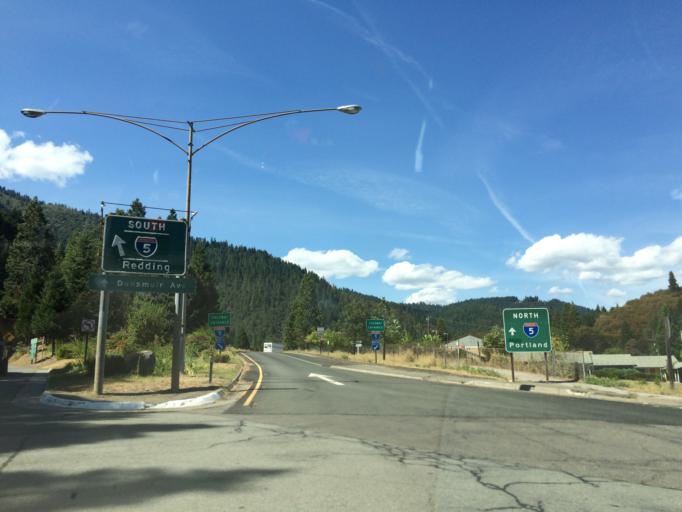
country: US
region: California
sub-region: Siskiyou County
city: Dunsmuir
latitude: 41.2174
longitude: -122.2733
